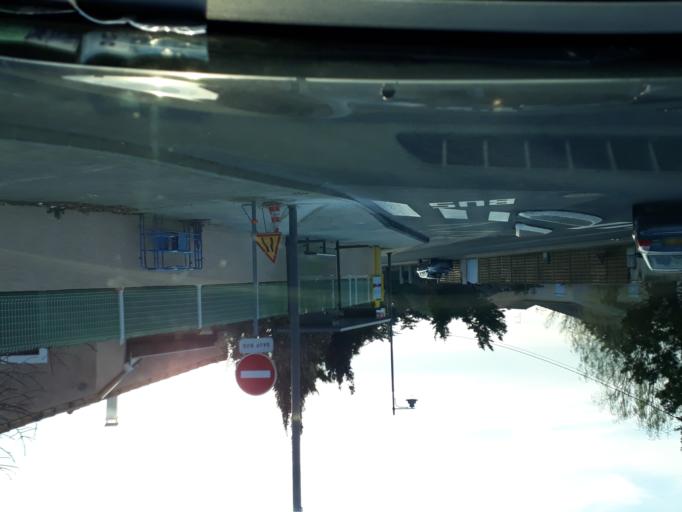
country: FR
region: Languedoc-Roussillon
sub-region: Departement de l'Herault
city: Marseillan
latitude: 43.3354
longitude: 3.5312
